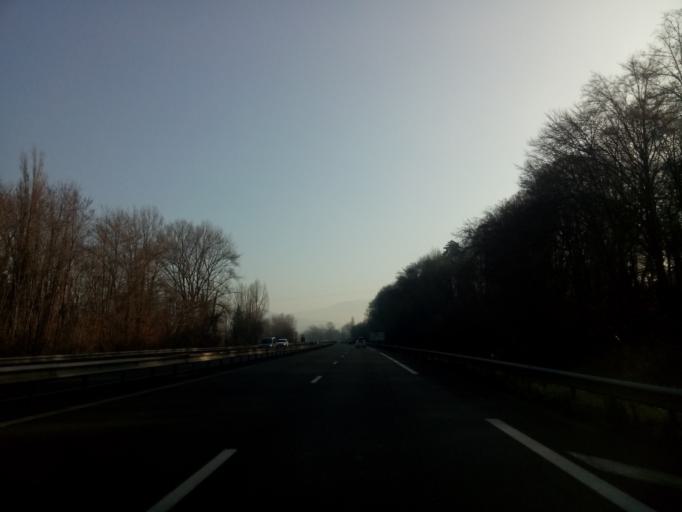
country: FR
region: Rhone-Alpes
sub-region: Departement de l'Isere
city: Romagnieu
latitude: 45.5750
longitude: 5.6420
